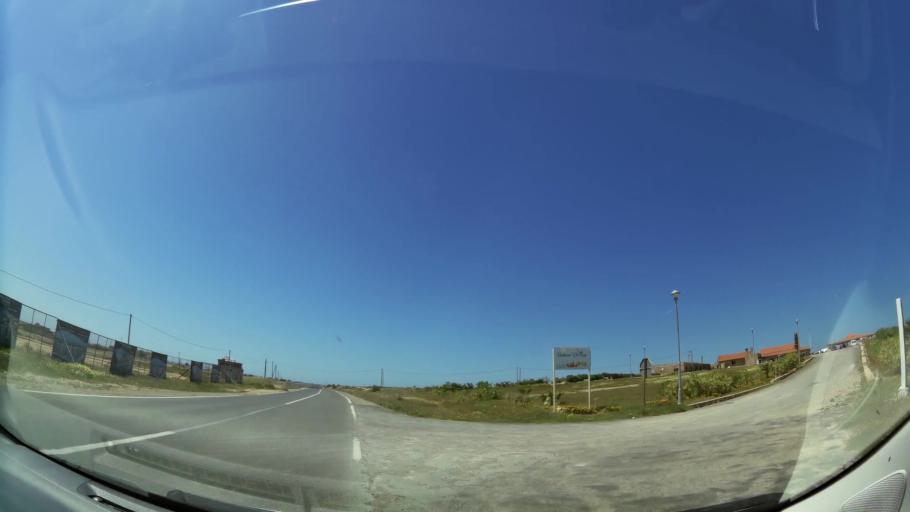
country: MA
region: Oriental
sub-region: Berkane-Taourirt
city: Madagh
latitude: 35.1308
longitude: -2.3974
